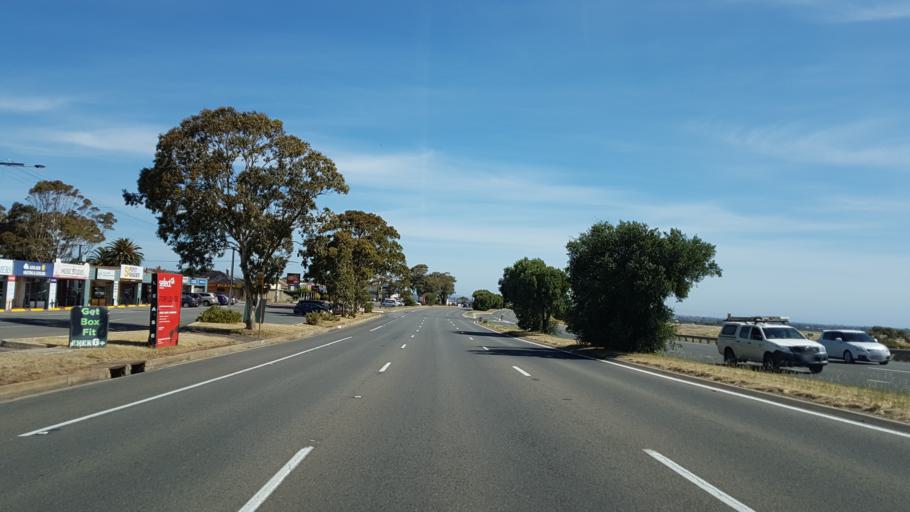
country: AU
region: South Australia
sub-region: Marion
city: Trott Park
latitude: -35.0653
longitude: 138.5550
